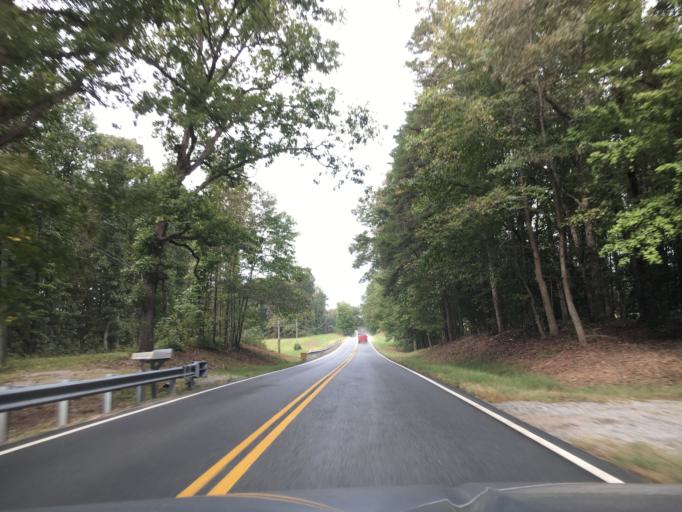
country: US
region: Virginia
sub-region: Goochland County
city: Goochland
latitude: 37.7352
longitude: -77.8404
